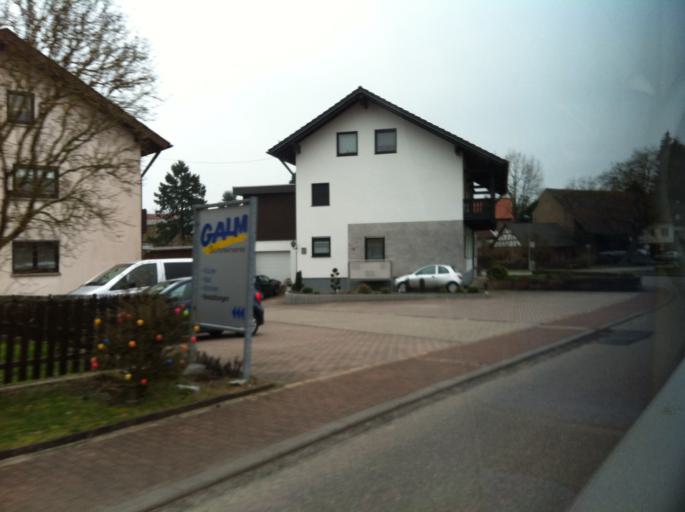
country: DE
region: Baden-Wuerttemberg
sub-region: Karlsruhe Region
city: Fahrenbach
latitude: 49.4531
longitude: 9.1631
